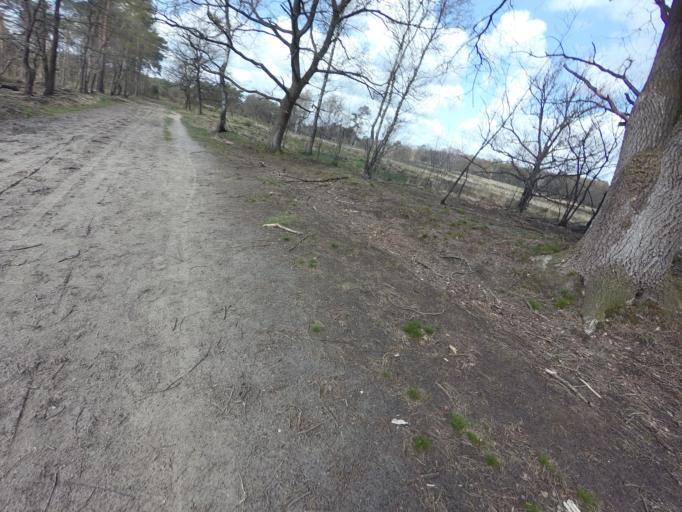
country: NL
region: Limburg
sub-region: Gemeente Roerdalen
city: Herkenbosch
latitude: 51.1670
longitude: 6.0947
